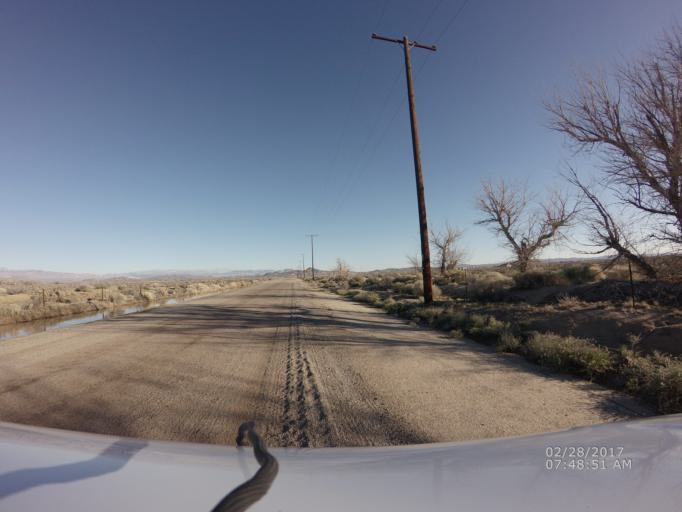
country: US
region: California
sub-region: Kern County
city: Rosamond
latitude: 34.8173
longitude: -118.1848
